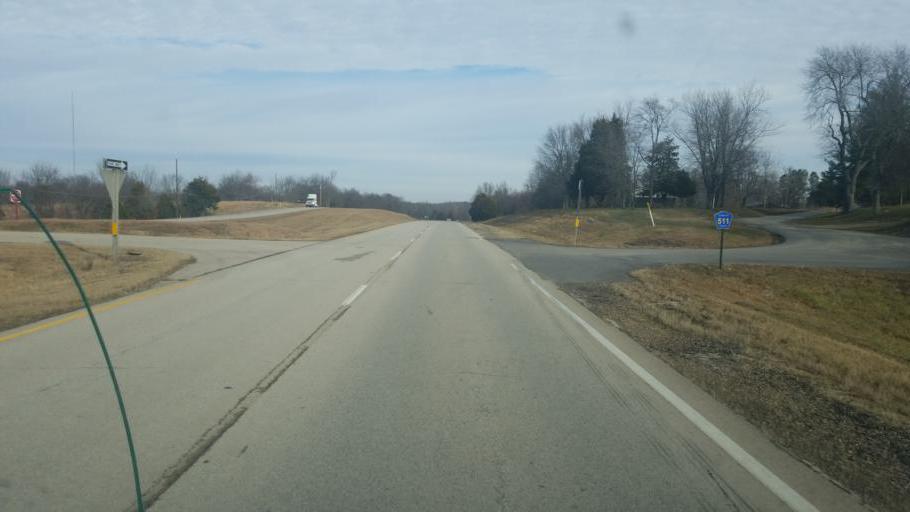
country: US
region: Missouri
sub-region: Stoddard County
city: Bloomfield
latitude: 36.8508
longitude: -89.9398
